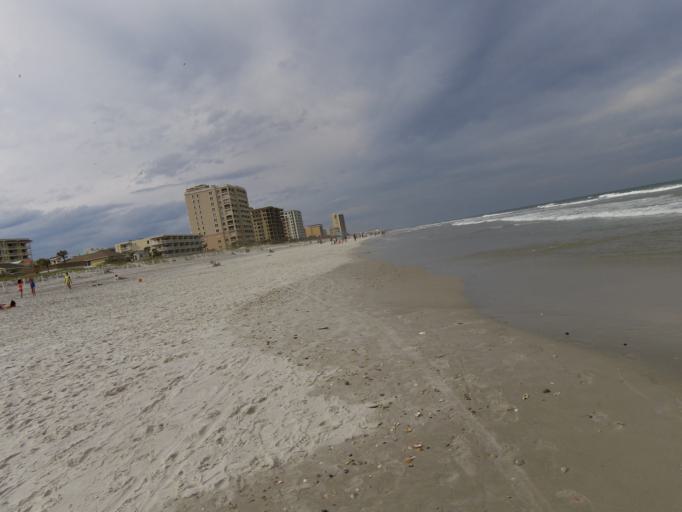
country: US
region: Florida
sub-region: Duval County
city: Jacksonville Beach
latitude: 30.2979
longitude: -81.3899
